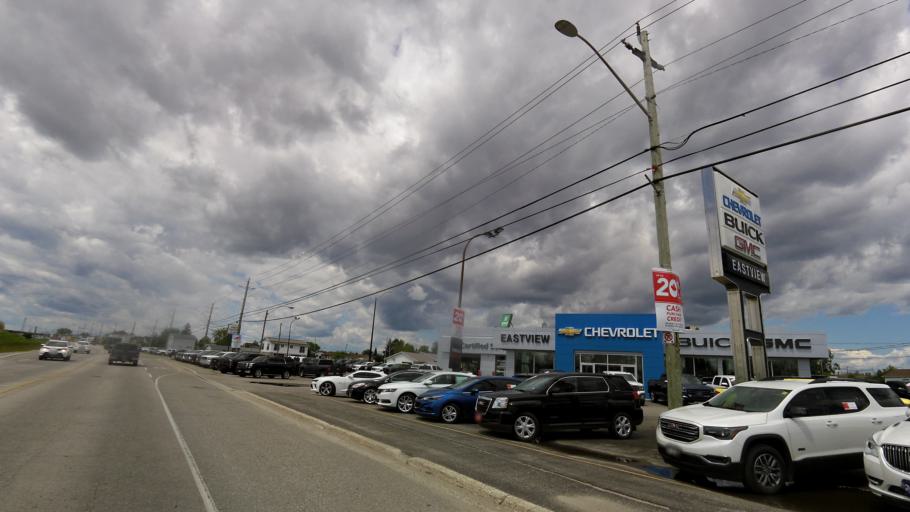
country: CA
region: Ontario
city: Kapuskasing
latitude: 49.4072
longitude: -82.3968
